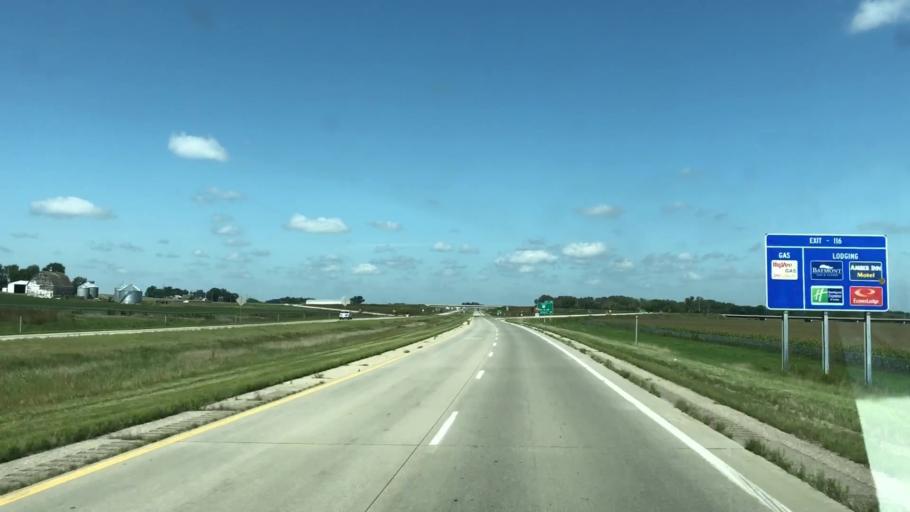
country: US
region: Iowa
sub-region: Plymouth County
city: Le Mars
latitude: 42.7564
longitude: -96.2092
